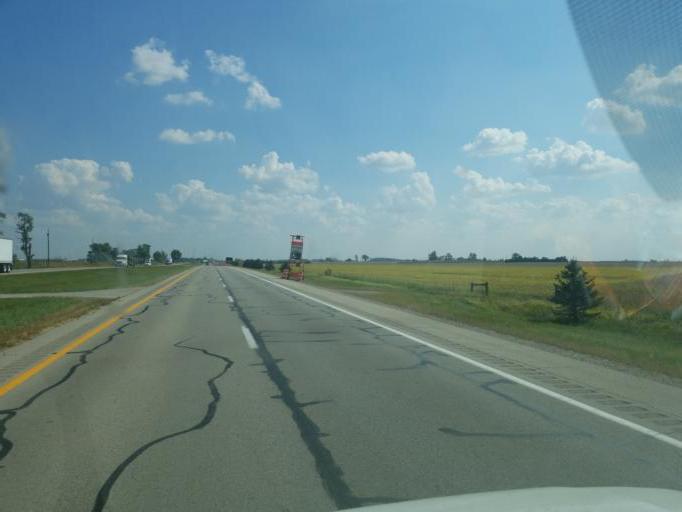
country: US
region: Ohio
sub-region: Van Wert County
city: Convoy
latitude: 40.9568
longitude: -84.7324
